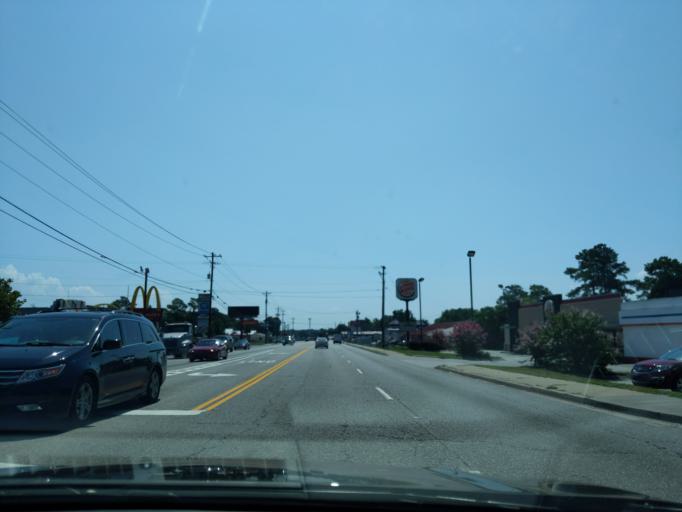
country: US
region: South Carolina
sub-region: Lexington County
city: Oak Grove
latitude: 33.9739
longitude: -81.1564
